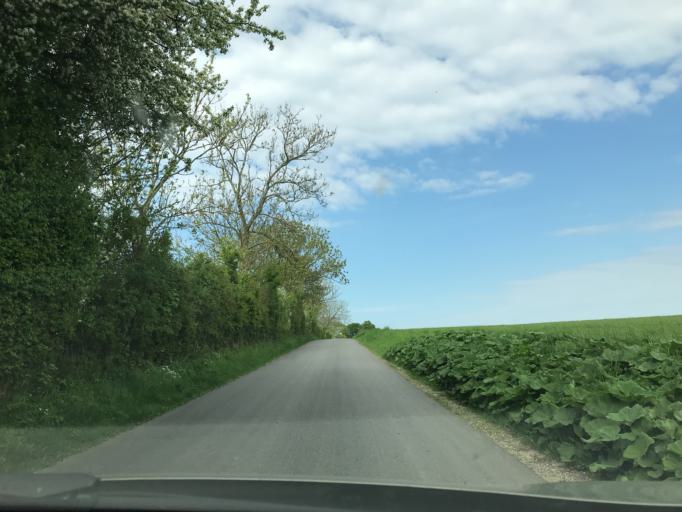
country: DK
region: South Denmark
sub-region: Middelfart Kommune
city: Norre Aby
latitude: 55.3664
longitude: 9.8379
